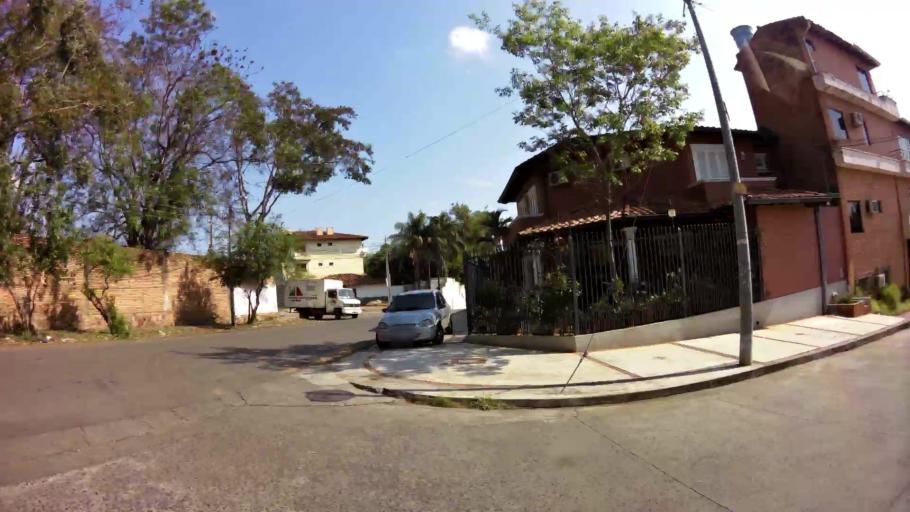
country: PY
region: Asuncion
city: Asuncion
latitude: -25.3242
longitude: -57.6320
